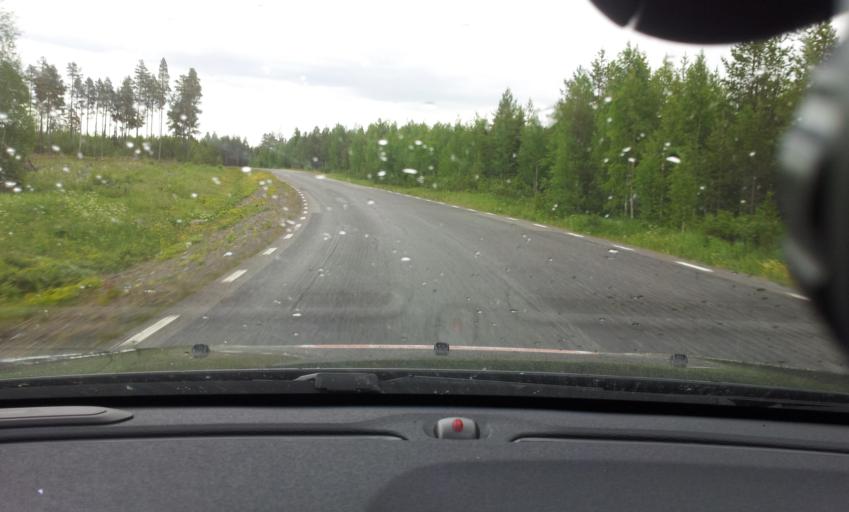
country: SE
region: Jaemtland
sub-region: OEstersunds Kommun
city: Brunflo
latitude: 63.1951
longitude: 14.8948
